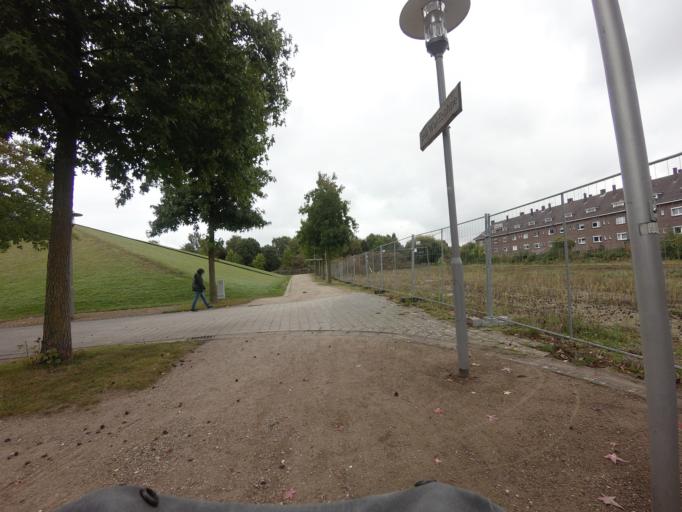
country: DE
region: North Rhine-Westphalia
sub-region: Regierungsbezirk Munster
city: Gronau
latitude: 52.2126
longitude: 7.0288
